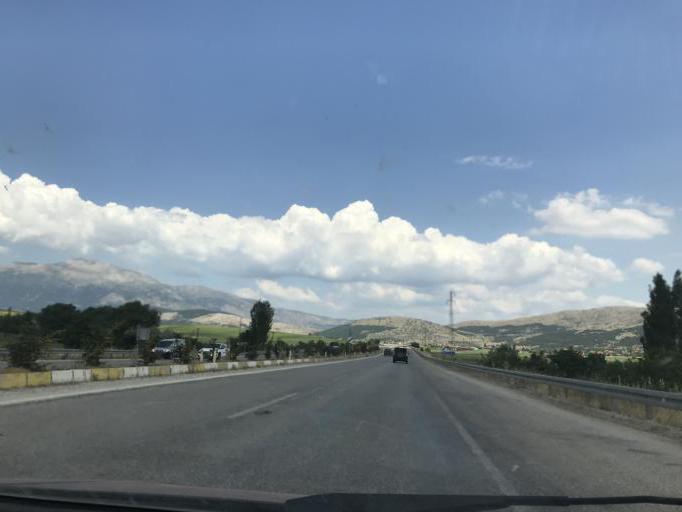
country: TR
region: Denizli
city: Serinhisar
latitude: 37.6159
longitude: 29.1736
